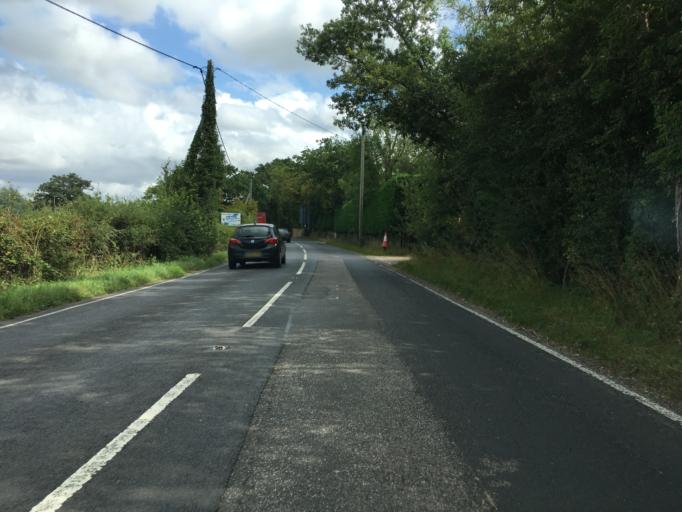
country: GB
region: England
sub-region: Kent
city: Tenterden
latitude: 51.1052
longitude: 0.6444
